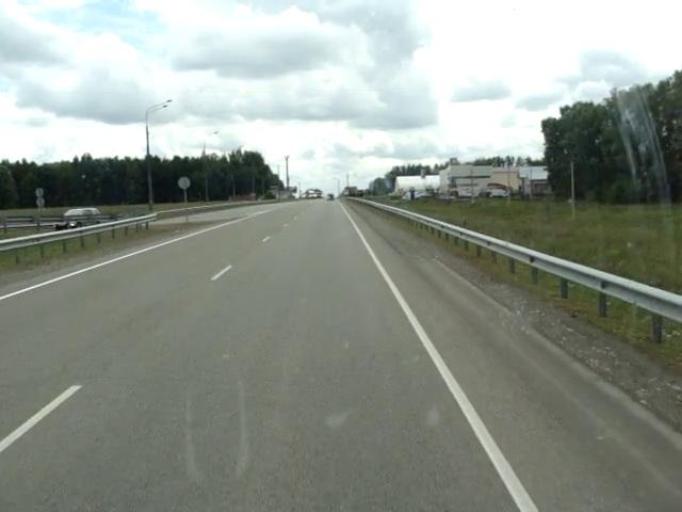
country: RU
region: Altai Krai
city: Zarya
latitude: 52.5771
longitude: 85.1788
